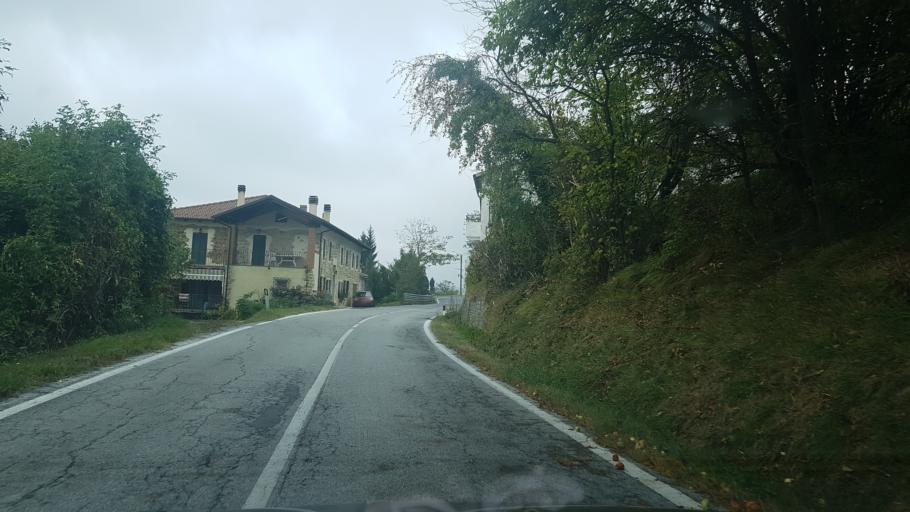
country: IT
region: Piedmont
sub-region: Provincia di Cuneo
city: Sale San Giovanni
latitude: 44.4158
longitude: 8.0895
